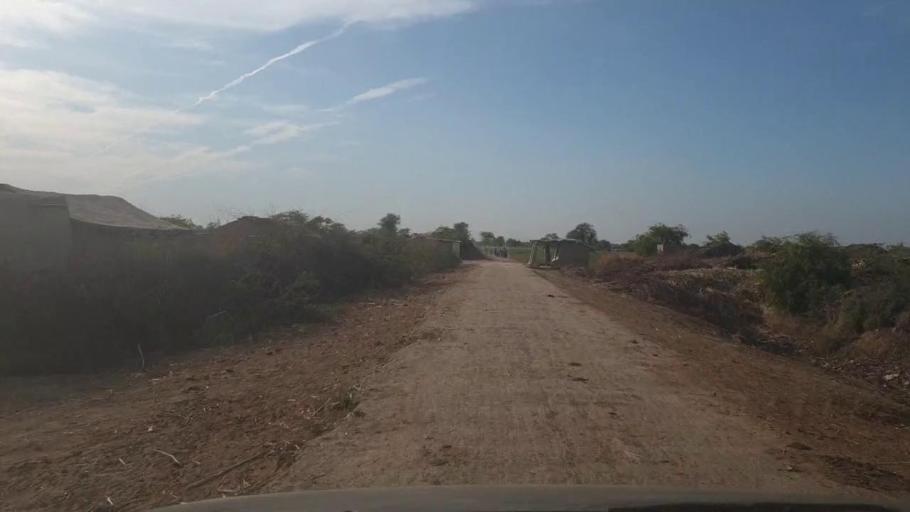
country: PK
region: Sindh
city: Samaro
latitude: 25.3351
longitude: 69.2359
